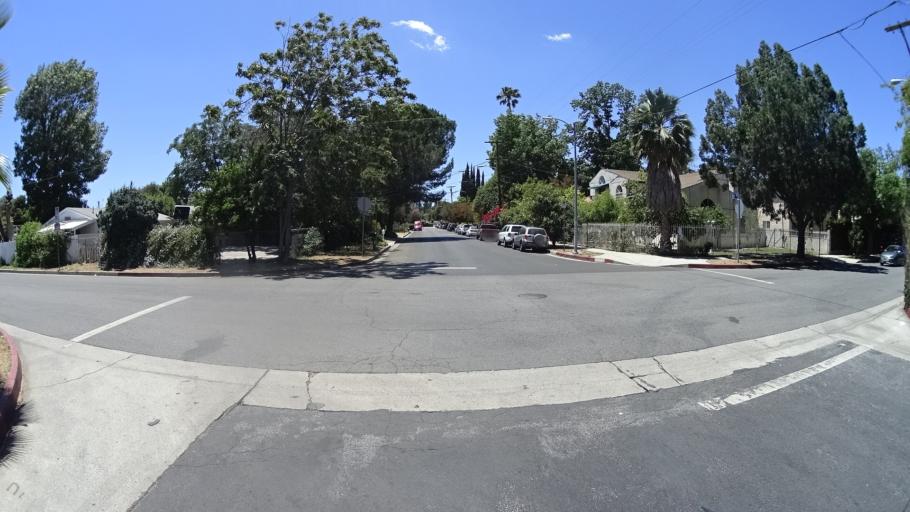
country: US
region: California
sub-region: Los Angeles County
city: Van Nuys
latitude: 34.1985
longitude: -118.4684
